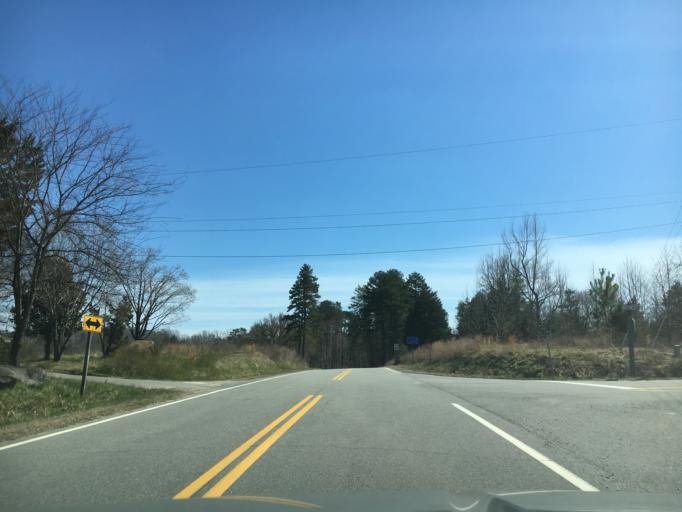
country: US
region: Virginia
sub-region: Halifax County
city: Halifax
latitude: 36.7608
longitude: -78.9102
